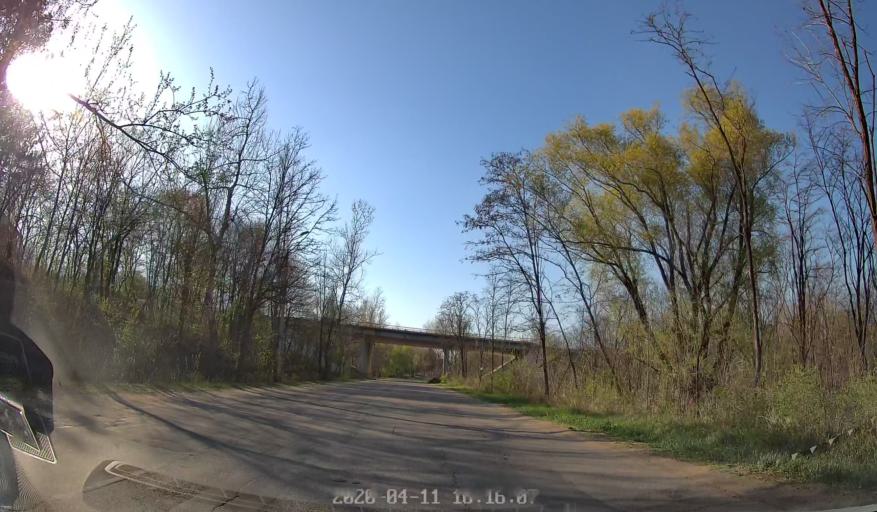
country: MD
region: Chisinau
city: Vadul lui Voda
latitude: 47.0838
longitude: 29.0894
